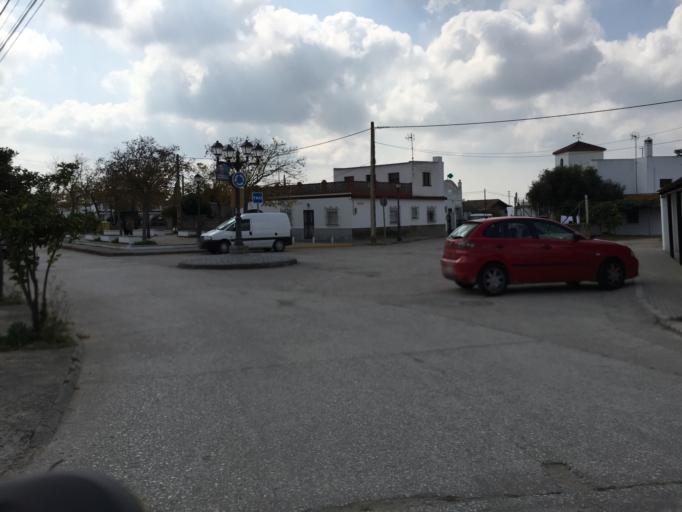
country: ES
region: Andalusia
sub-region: Provincia de Cadiz
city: Benalup-Casas Viejas
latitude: 36.3161
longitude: -5.8851
